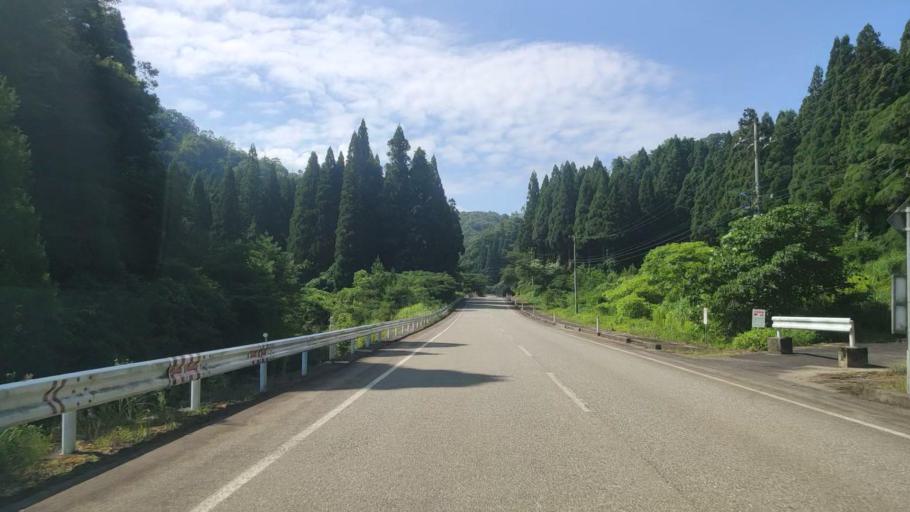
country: JP
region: Ishikawa
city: Komatsu
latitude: 36.3214
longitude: 136.5325
